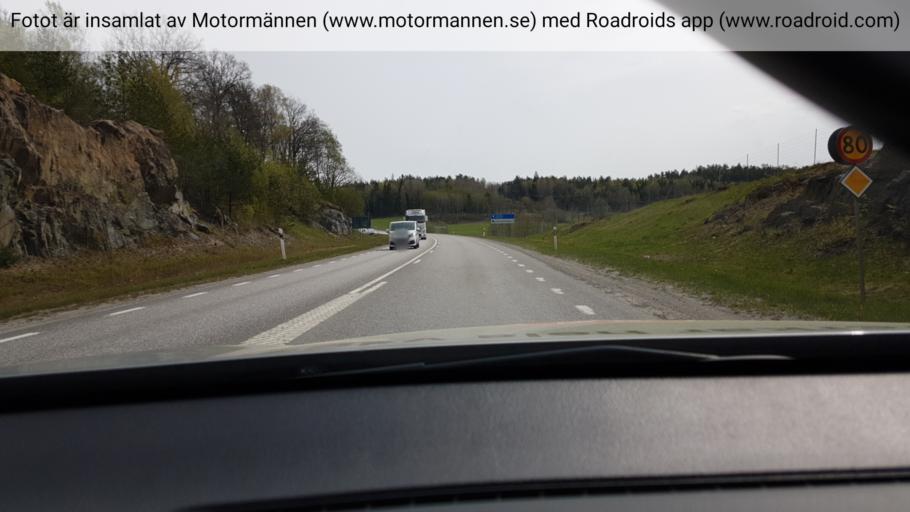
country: SE
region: Stockholm
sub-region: Huddinge Kommun
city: Huddinge
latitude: 59.1957
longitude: 18.0122
